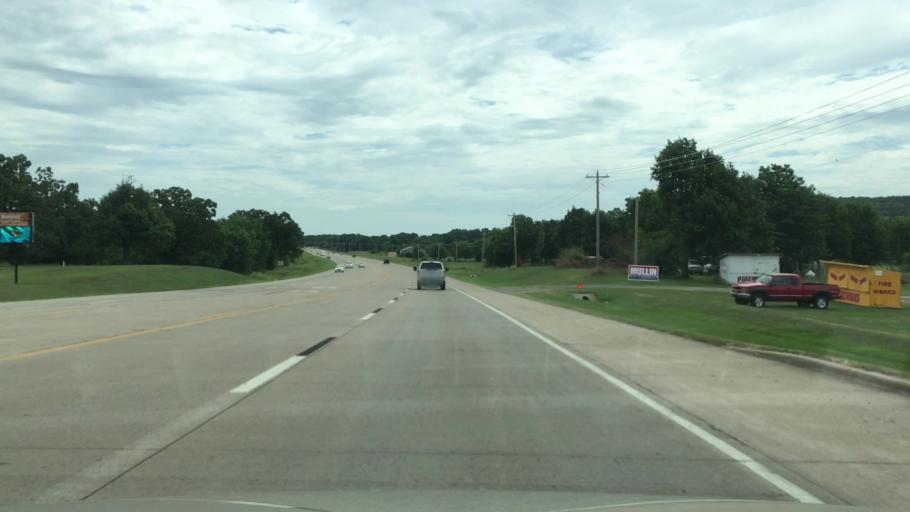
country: US
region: Oklahoma
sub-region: Cherokee County
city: Park Hill
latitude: 35.8189
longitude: -95.0556
